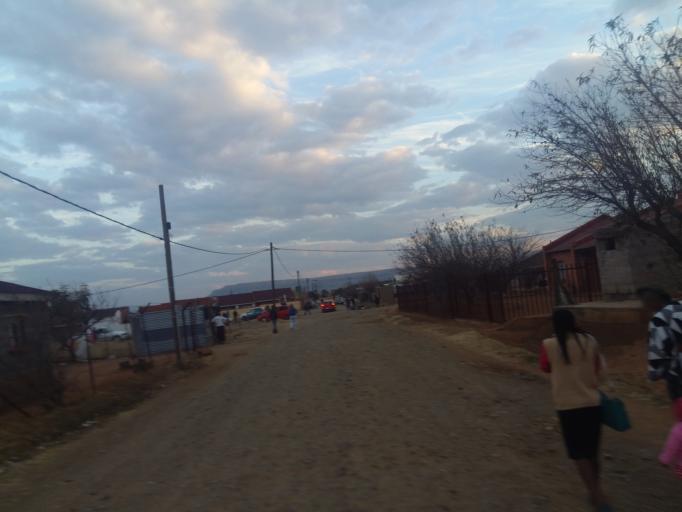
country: LS
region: Maseru
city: Maseru
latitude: -29.3824
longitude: 27.5317
